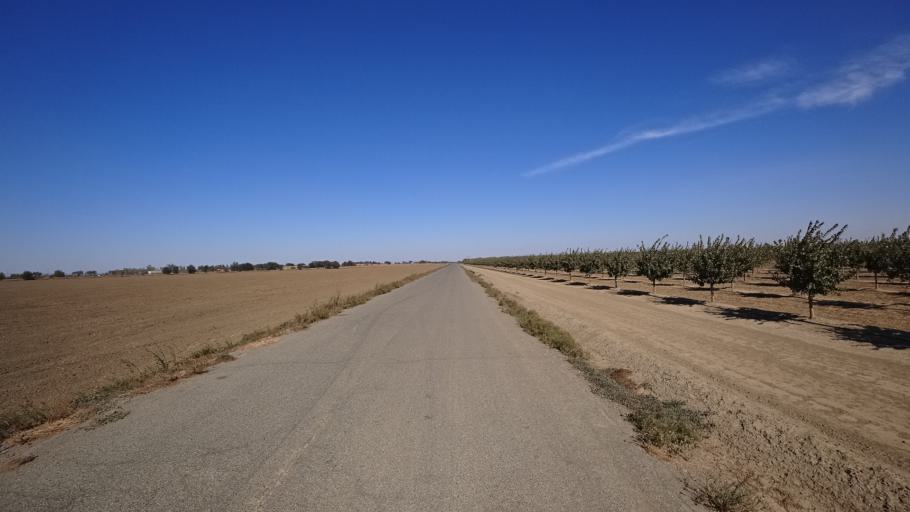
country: US
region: California
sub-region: Yolo County
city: Woodland
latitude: 38.6350
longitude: -121.7571
